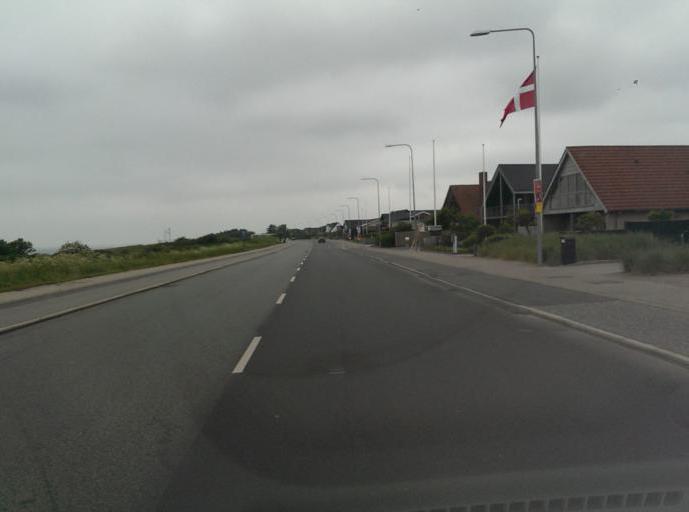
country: DK
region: South Denmark
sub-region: Fano Kommune
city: Nordby
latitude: 55.4962
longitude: 8.3977
